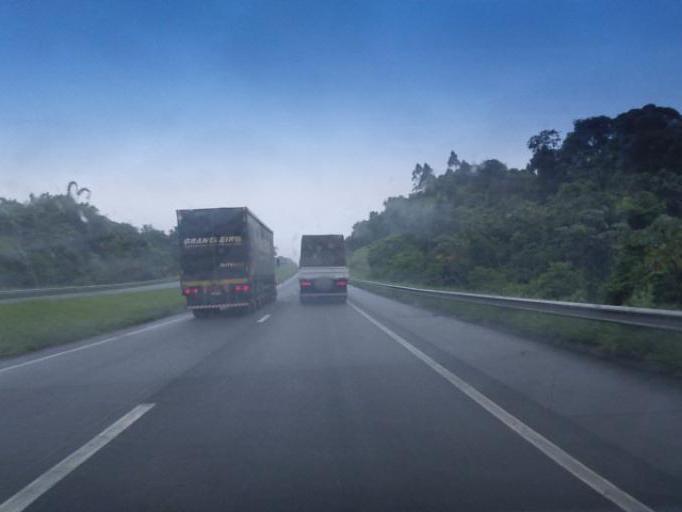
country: BR
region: Sao Paulo
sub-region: Pariquera-Acu
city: Pariquera Acu
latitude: -24.6175
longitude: -47.8902
